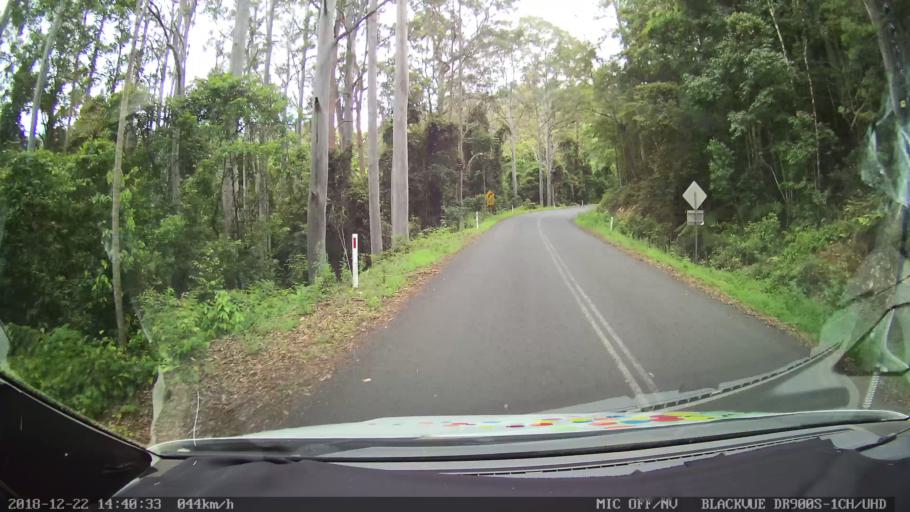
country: AU
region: New South Wales
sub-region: Bellingen
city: Dorrigo
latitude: -30.1512
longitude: 152.5888
